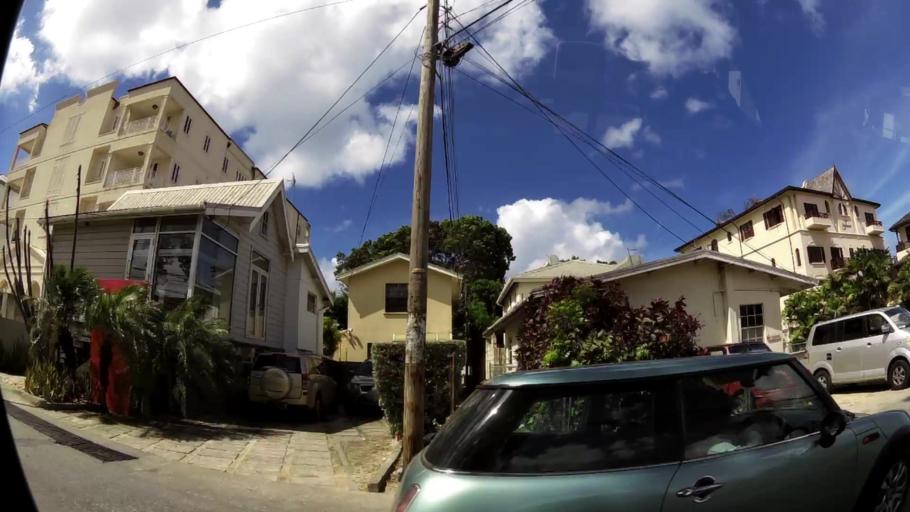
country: BB
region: Saint James
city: Holetown
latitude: 13.1652
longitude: -59.6366
